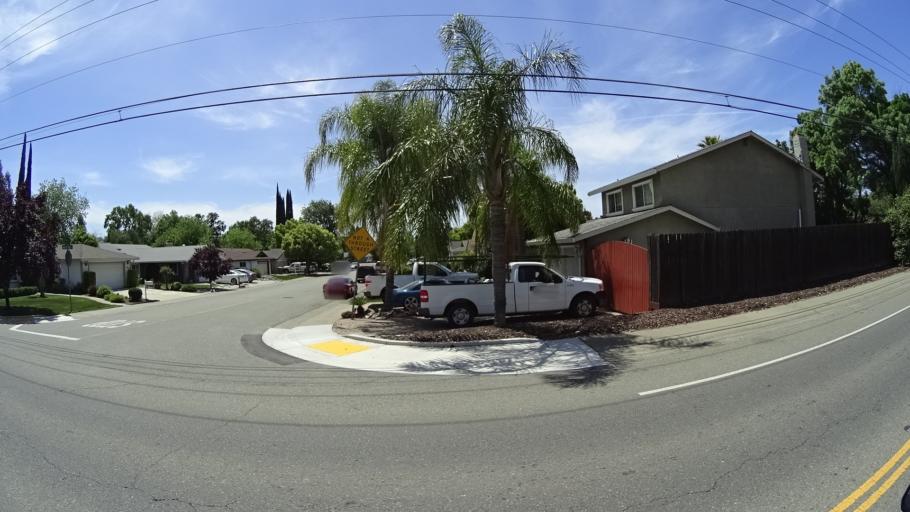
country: US
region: California
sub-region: Placer County
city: Rocklin
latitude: 38.7972
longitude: -121.2369
